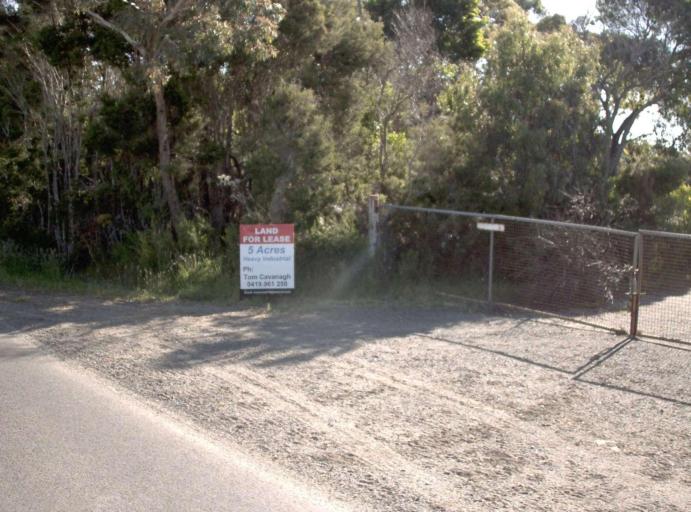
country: AU
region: Victoria
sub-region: Latrobe
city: Morwell
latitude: -38.7068
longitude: 146.3975
